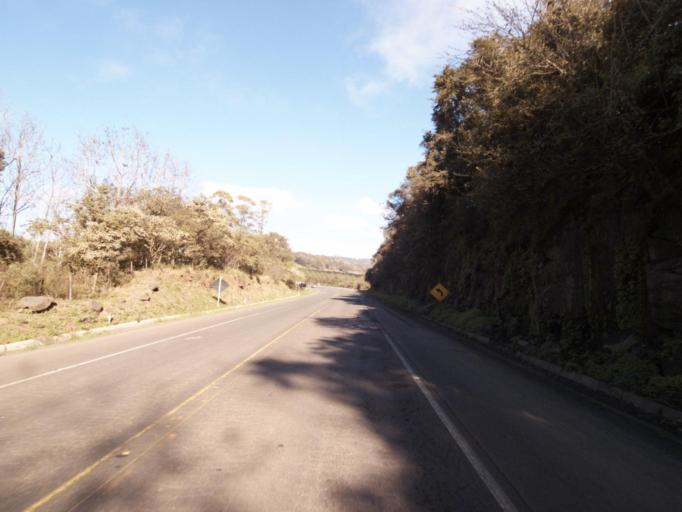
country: BR
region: Rio Grande do Sul
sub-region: Frederico Westphalen
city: Frederico Westphalen
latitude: -27.0468
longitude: -53.2275
